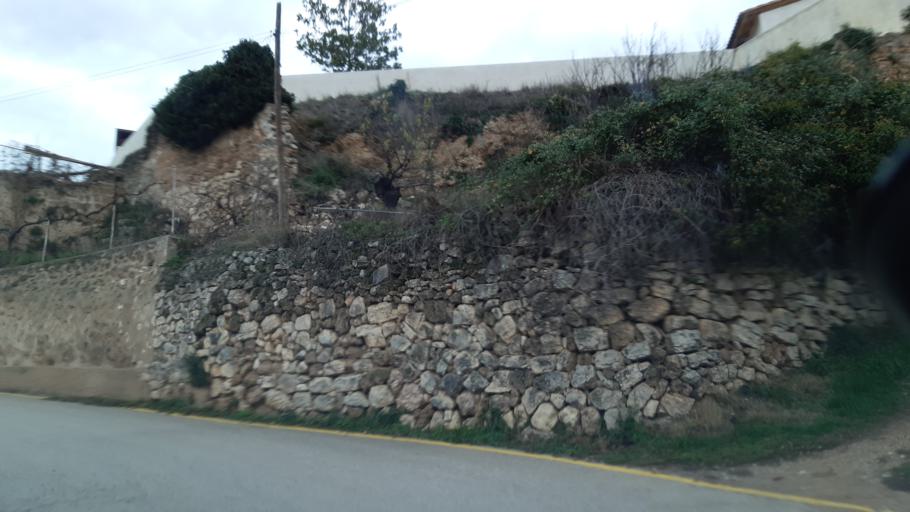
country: ES
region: Aragon
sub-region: Provincia de Teruel
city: Valderrobres
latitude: 40.8301
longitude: 0.1828
